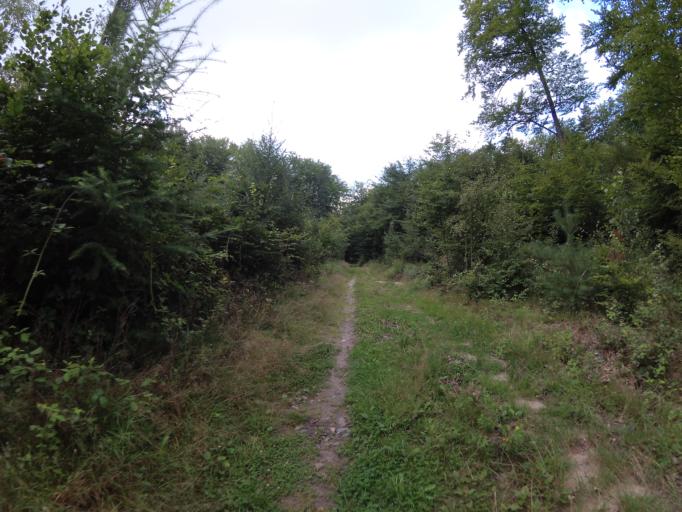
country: PL
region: Pomeranian Voivodeship
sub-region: Gdynia
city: Wielki Kack
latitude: 54.5061
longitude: 18.4399
